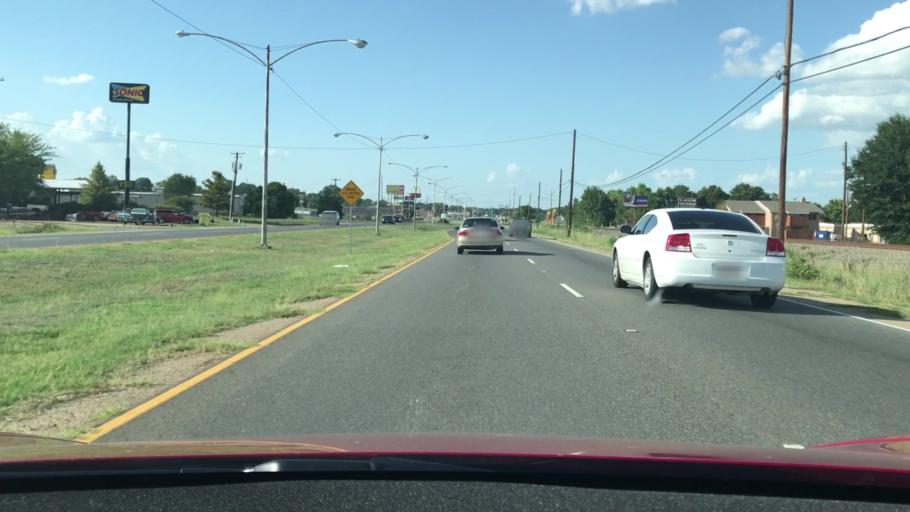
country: US
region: Louisiana
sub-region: Bossier Parish
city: Bossier City
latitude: 32.4377
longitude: -93.7822
